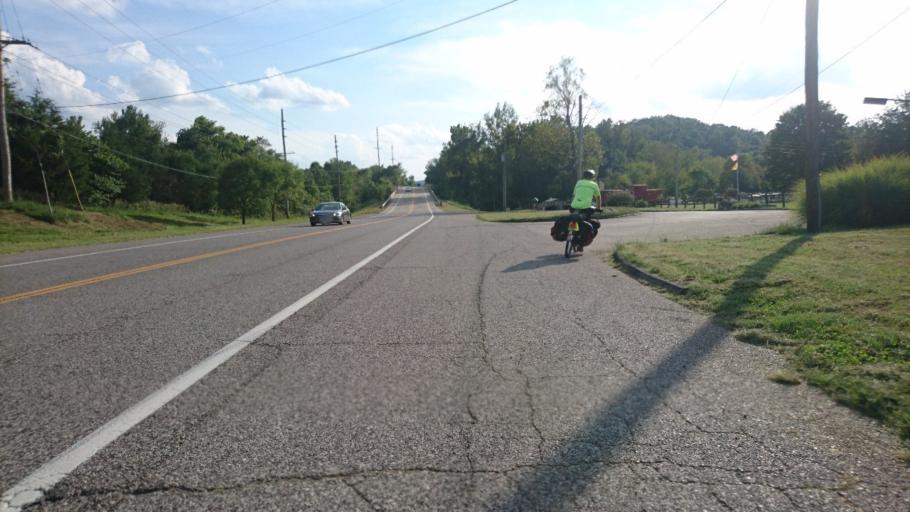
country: US
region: Missouri
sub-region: Franklin County
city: Pacific
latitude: 38.5011
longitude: -90.6878
